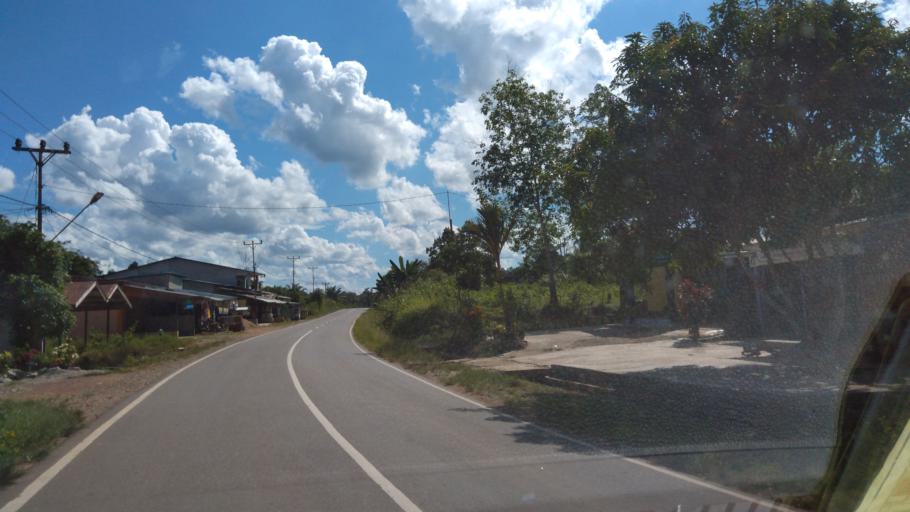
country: ID
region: West Kalimantan
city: Tayan
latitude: 0.2886
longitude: 110.2270
